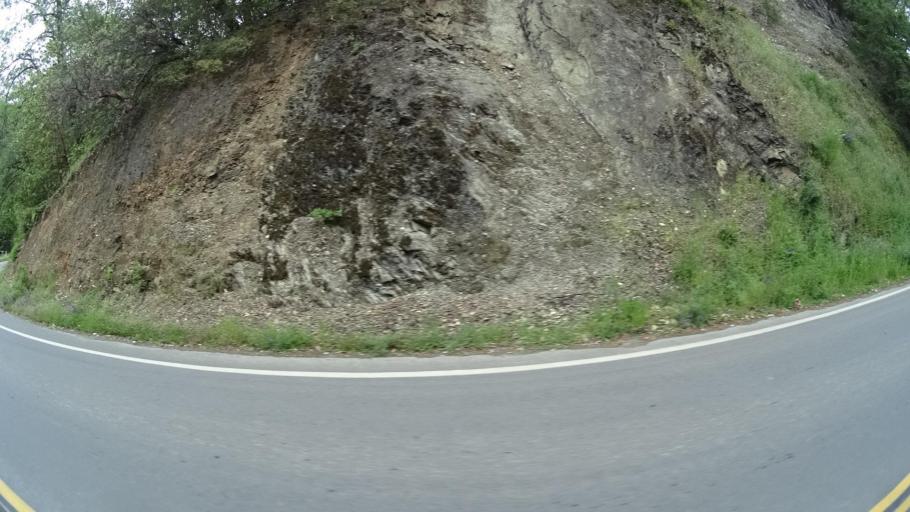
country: US
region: California
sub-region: Humboldt County
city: Willow Creek
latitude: 40.9410
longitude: -123.6269
